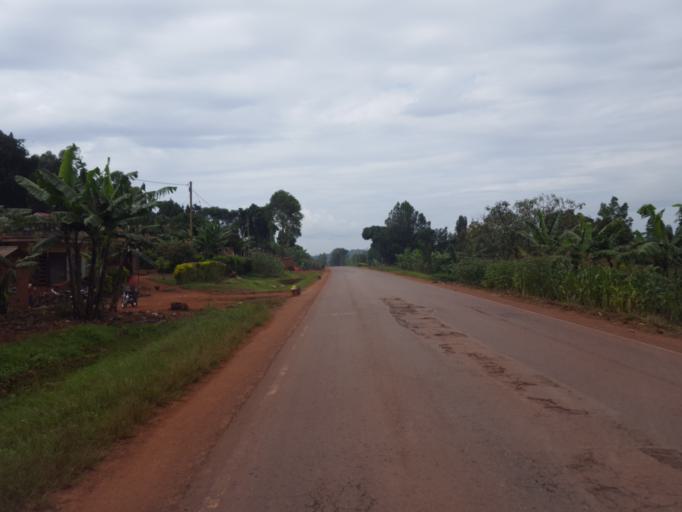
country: UG
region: Central Region
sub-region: Mityana District
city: Mityana
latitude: 0.6459
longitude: 32.0964
